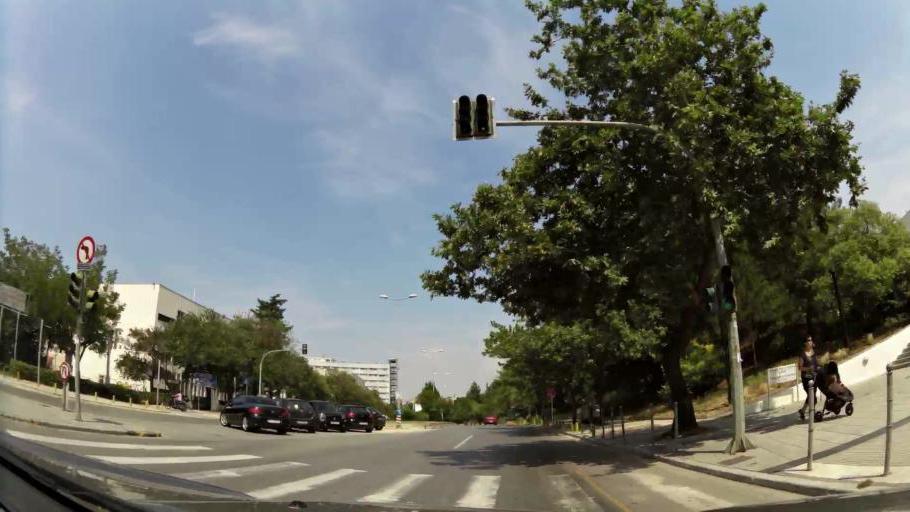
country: GR
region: Central Macedonia
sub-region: Nomos Thessalonikis
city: Agios Pavlos
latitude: 40.6323
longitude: 22.9601
